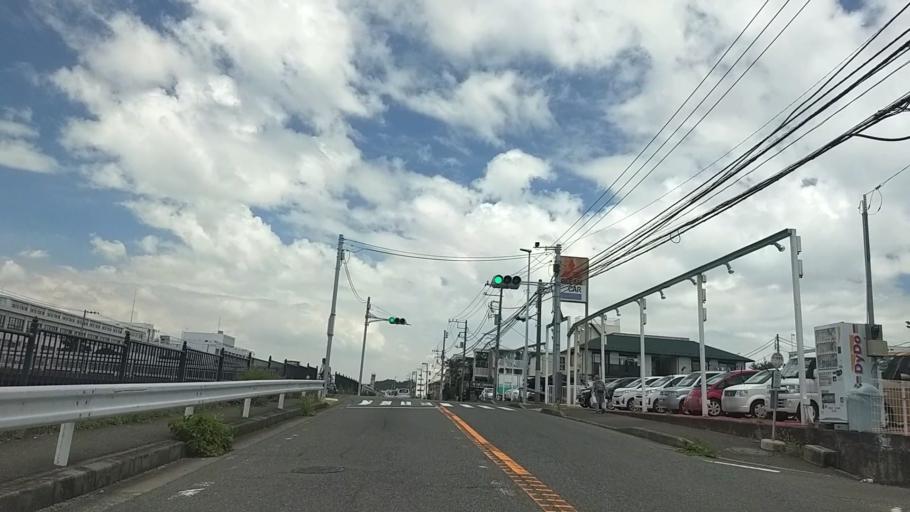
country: JP
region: Kanagawa
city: Fujisawa
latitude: 35.3356
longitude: 139.5119
